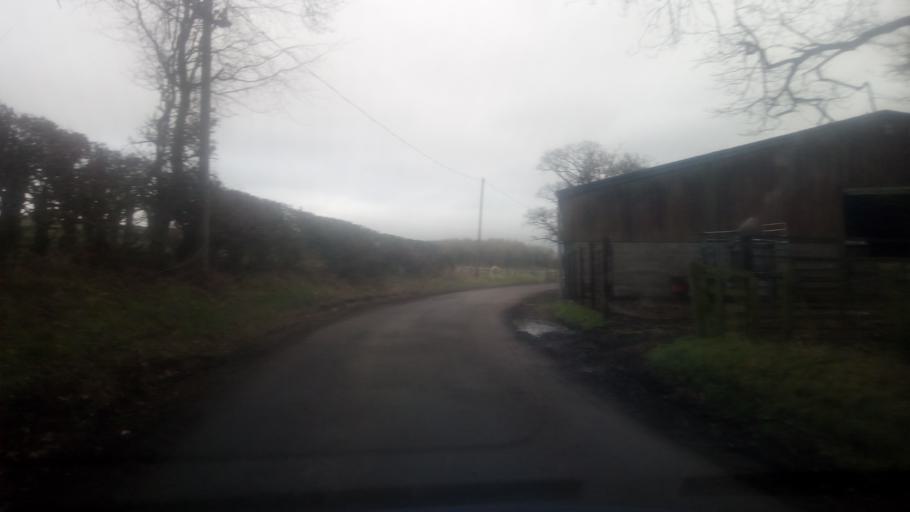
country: GB
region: Scotland
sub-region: The Scottish Borders
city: Jedburgh
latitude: 55.5268
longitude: -2.5155
